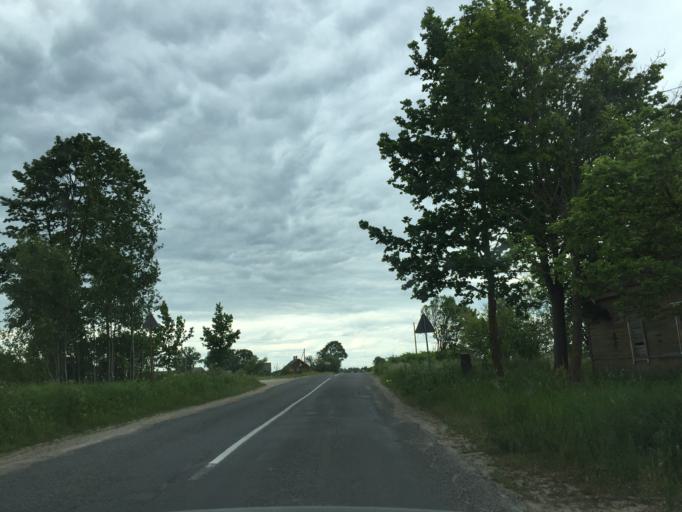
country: LV
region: Rezekne
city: Rezekne
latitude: 56.3566
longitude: 27.1463
